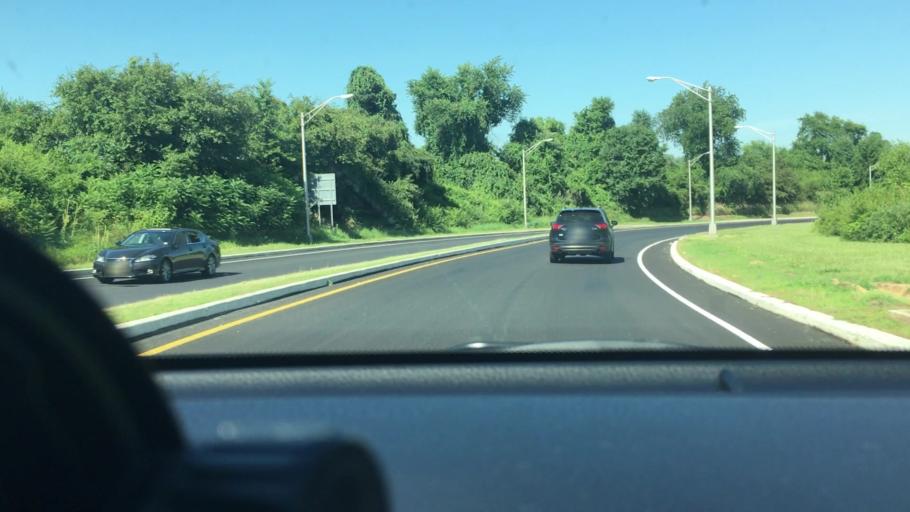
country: US
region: New Jersey
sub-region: Burlington County
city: Mount Laurel
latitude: 39.9683
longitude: -74.9123
